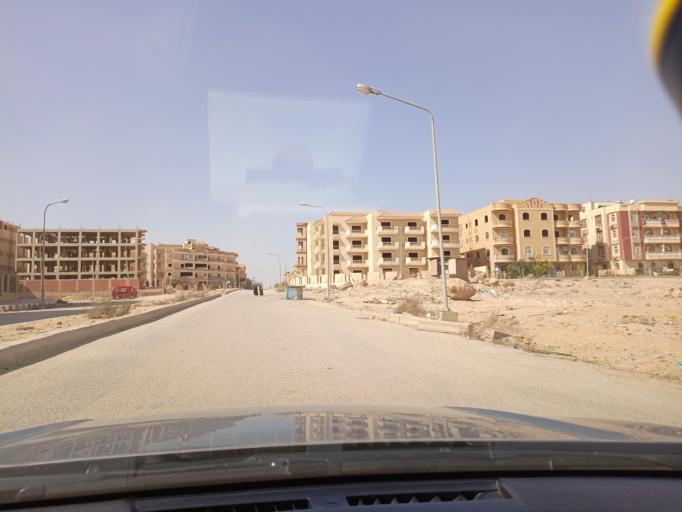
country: EG
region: Muhafazat al Qalyubiyah
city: Al Khankah
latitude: 30.2204
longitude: 31.4420
